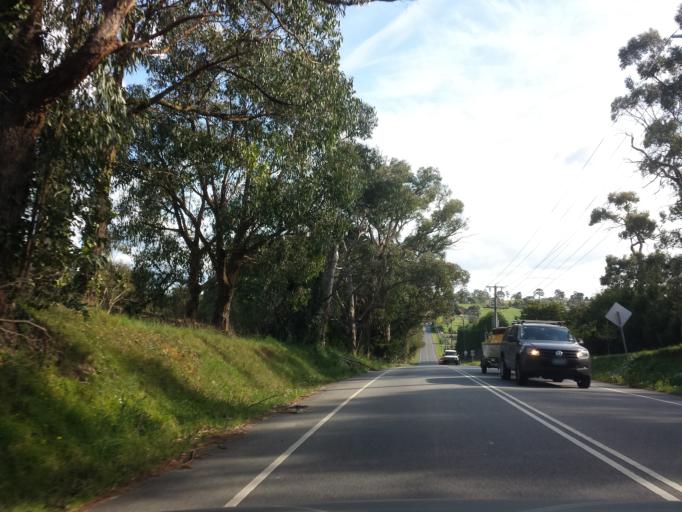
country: AU
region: Victoria
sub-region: Casey
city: Narre Warren North
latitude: -37.9756
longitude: 145.3602
